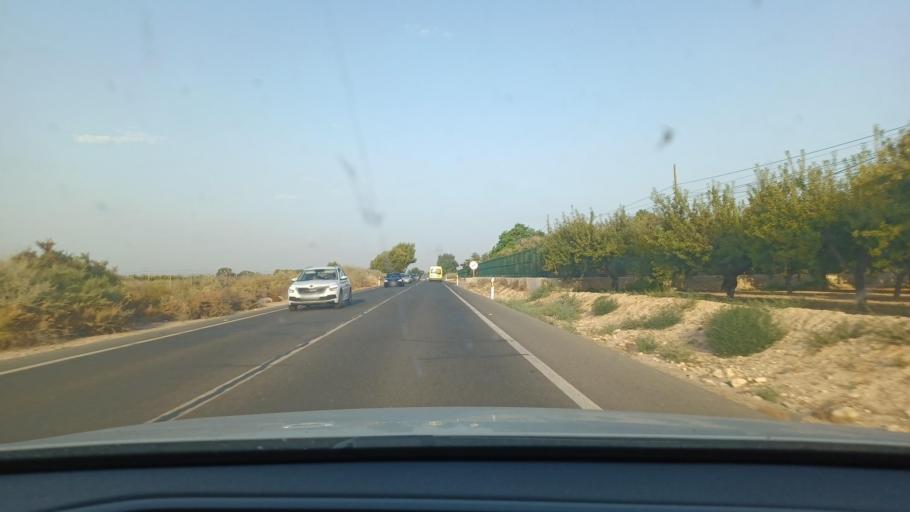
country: ES
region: Valencia
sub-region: Provincia de Alicante
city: Elche
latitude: 38.2825
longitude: -0.6311
